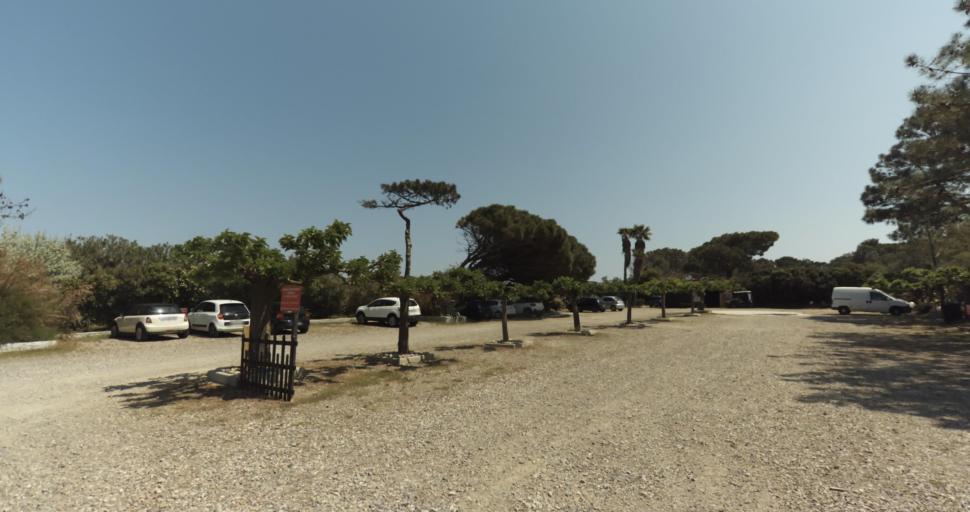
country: FR
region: Corsica
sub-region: Departement de la Haute-Corse
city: Biguglia
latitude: 42.6341
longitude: 9.4658
